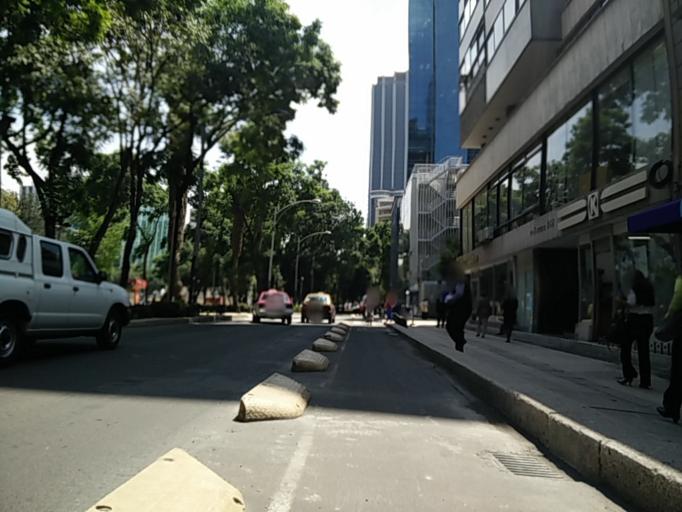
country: MX
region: Mexico City
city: Benito Juarez
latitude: 19.4258
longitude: -99.1691
